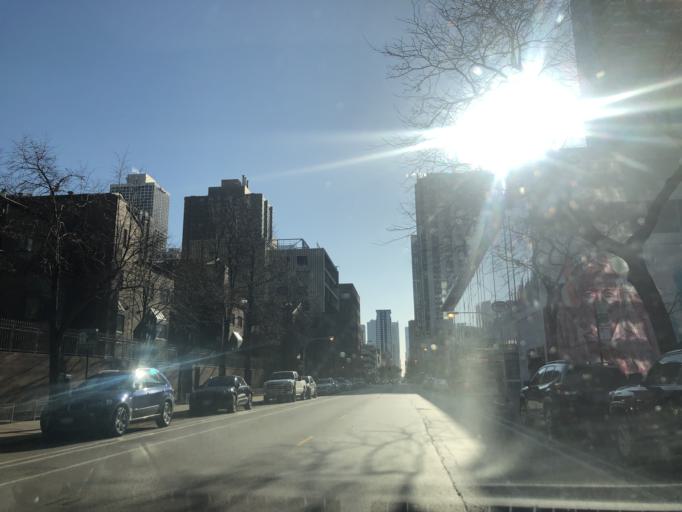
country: US
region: Illinois
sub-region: Cook County
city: Chicago
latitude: 41.9054
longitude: -87.6315
